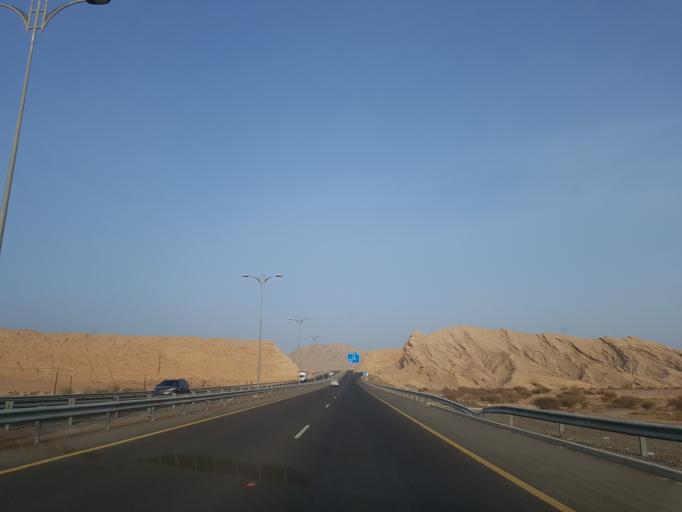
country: OM
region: Al Buraimi
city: Al Buraymi
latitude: 24.2333
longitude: 55.9435
